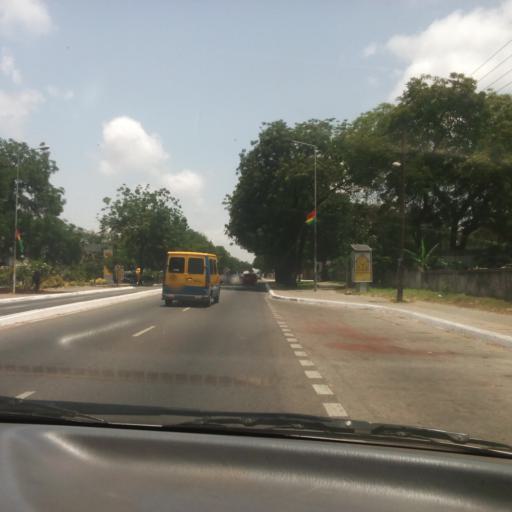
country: GH
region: Greater Accra
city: Accra
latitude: 5.5619
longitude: -0.1956
